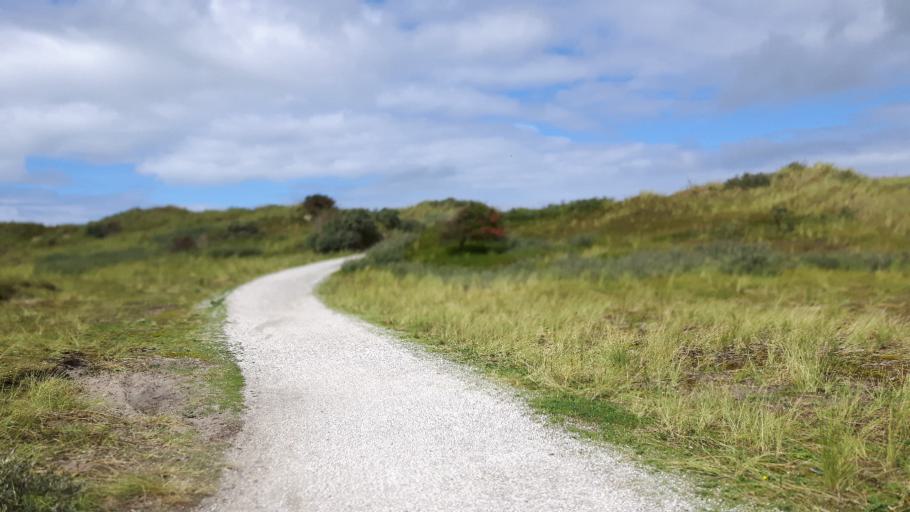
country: NL
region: Friesland
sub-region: Gemeente Ameland
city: Hollum
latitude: 53.4515
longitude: 5.6212
